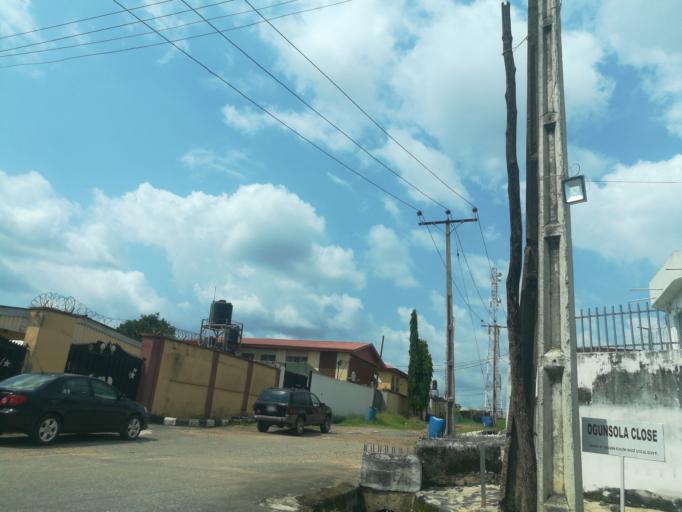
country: NG
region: Oyo
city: Ibadan
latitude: 7.3650
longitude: 3.8536
